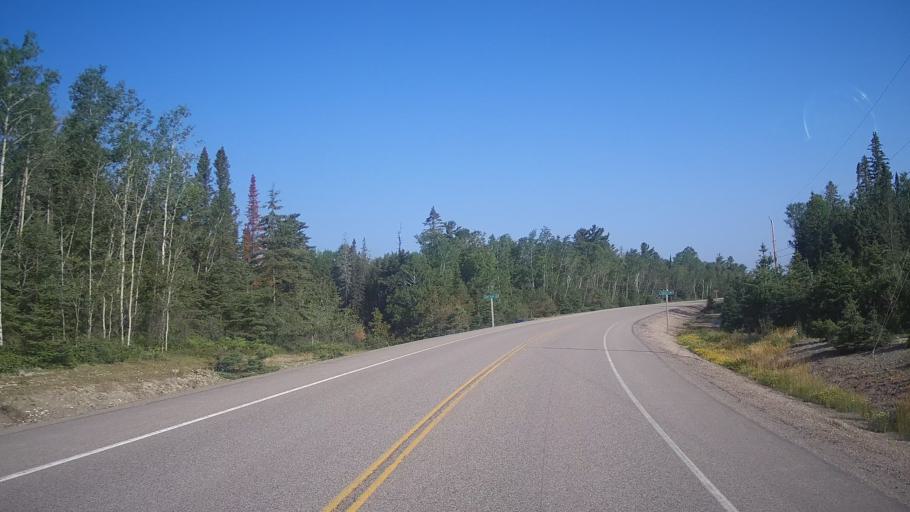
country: CA
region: Ontario
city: Rayside-Balfour
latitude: 46.7327
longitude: -81.5903
